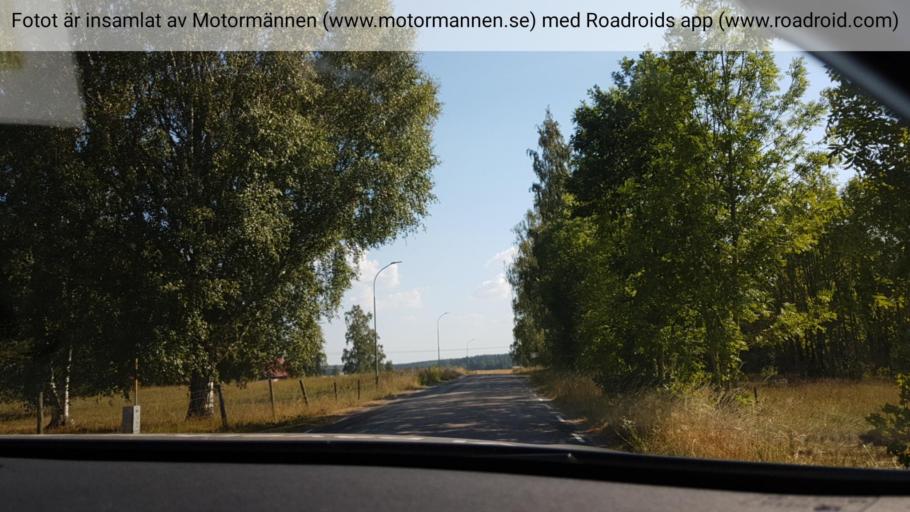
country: SE
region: Vaestra Goetaland
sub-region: Mariestads Kommun
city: Mariestad
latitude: 58.5924
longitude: 13.8625
